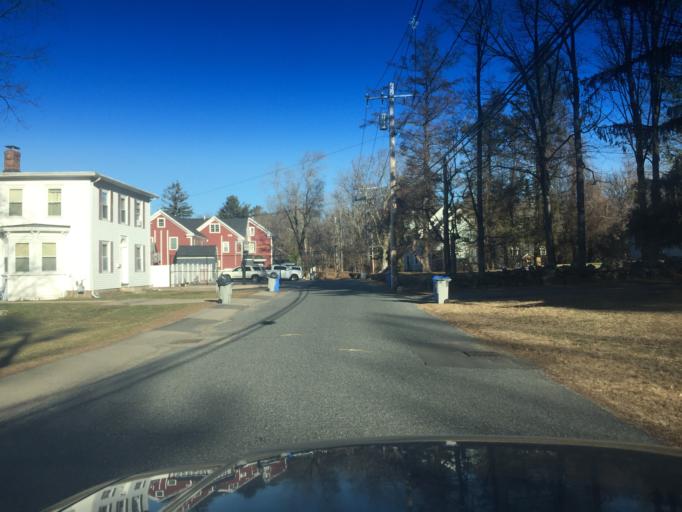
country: US
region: Massachusetts
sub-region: Middlesex County
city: Holliston
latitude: 42.1998
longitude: -71.4205
